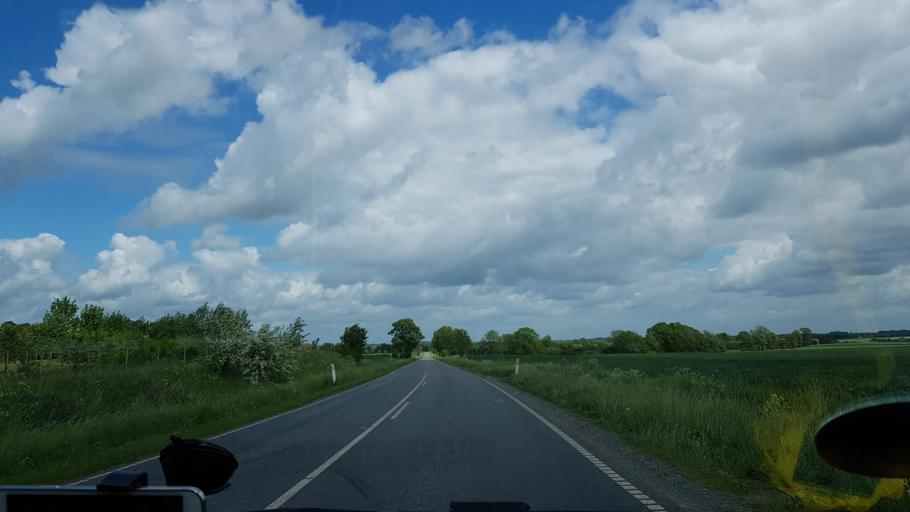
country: DK
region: South Denmark
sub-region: Kolding Kommune
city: Christiansfeld
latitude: 55.3323
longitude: 9.4479
